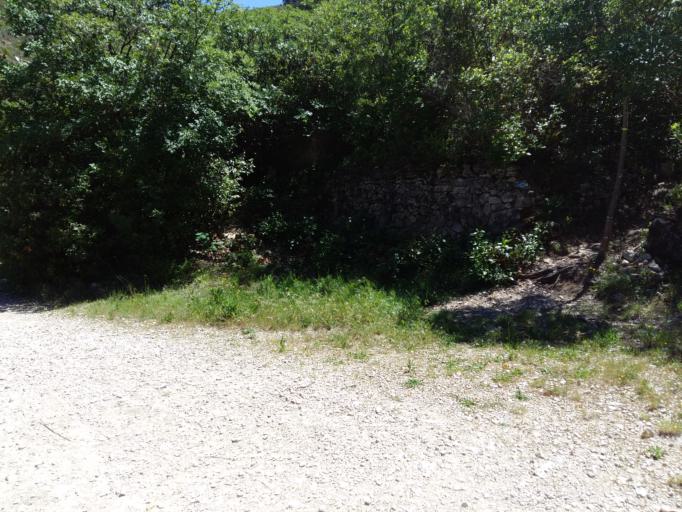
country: FR
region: Provence-Alpes-Cote d'Azur
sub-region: Departement des Bouches-du-Rhone
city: Marseille 11
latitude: 43.2753
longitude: 5.4662
